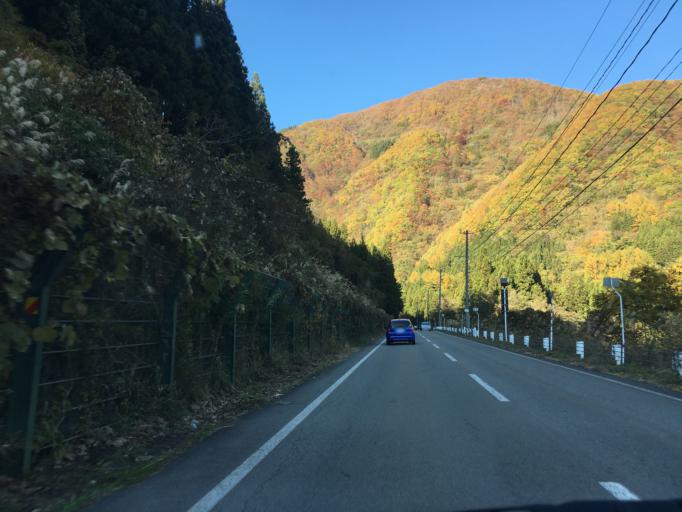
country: JP
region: Fukushima
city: Inawashiro
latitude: 37.2899
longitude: 139.9609
